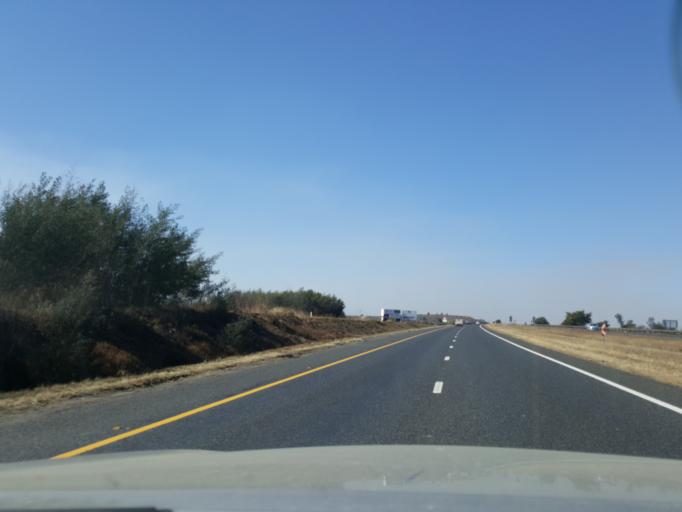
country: ZA
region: Gauteng
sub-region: City of Tshwane Metropolitan Municipality
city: Bronkhorstspruit
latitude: -26.0167
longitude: 28.9503
